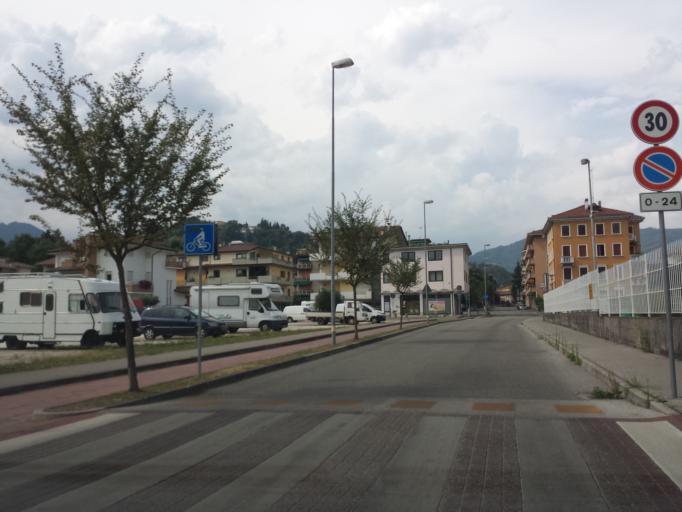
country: IT
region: Veneto
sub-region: Provincia di Vicenza
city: Valdagno
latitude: 45.6391
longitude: 11.3039
